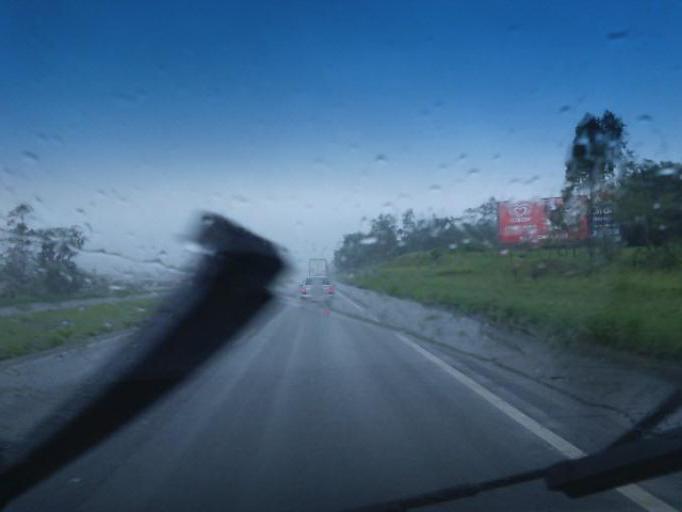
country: BR
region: Sao Paulo
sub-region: Pariquera-Acu
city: Pariquera Acu
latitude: -24.6291
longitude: -47.9023
